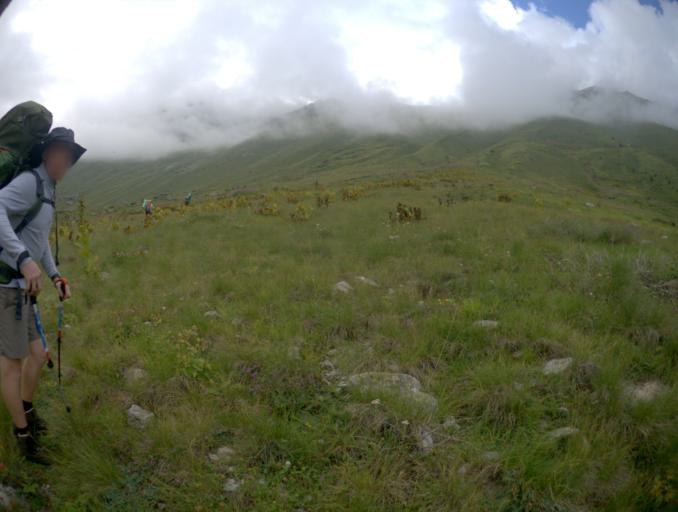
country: RU
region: Karachayevo-Cherkesiya
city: Uchkulan
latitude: 43.3340
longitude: 42.1200
